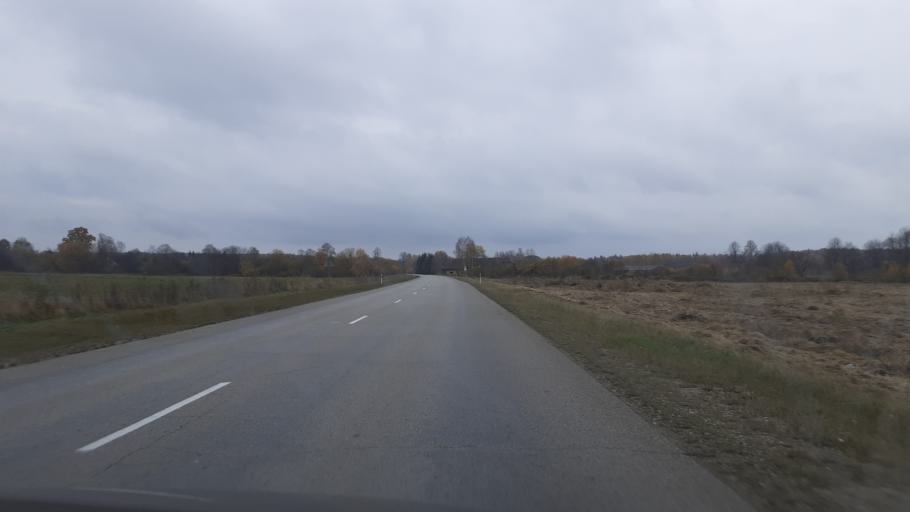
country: LV
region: Kuldigas Rajons
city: Kuldiga
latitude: 56.9377
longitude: 22.0286
